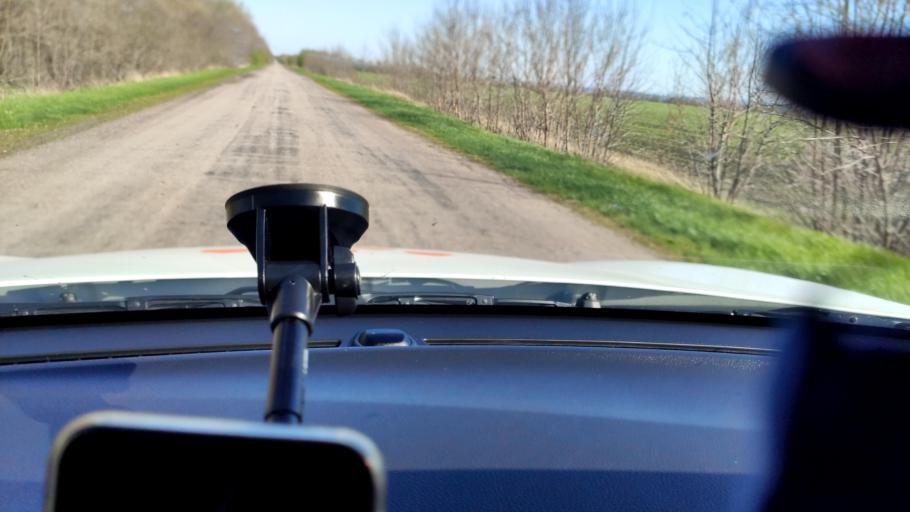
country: RU
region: Voronezj
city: Uryv-Pokrovka
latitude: 51.1415
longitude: 39.0740
